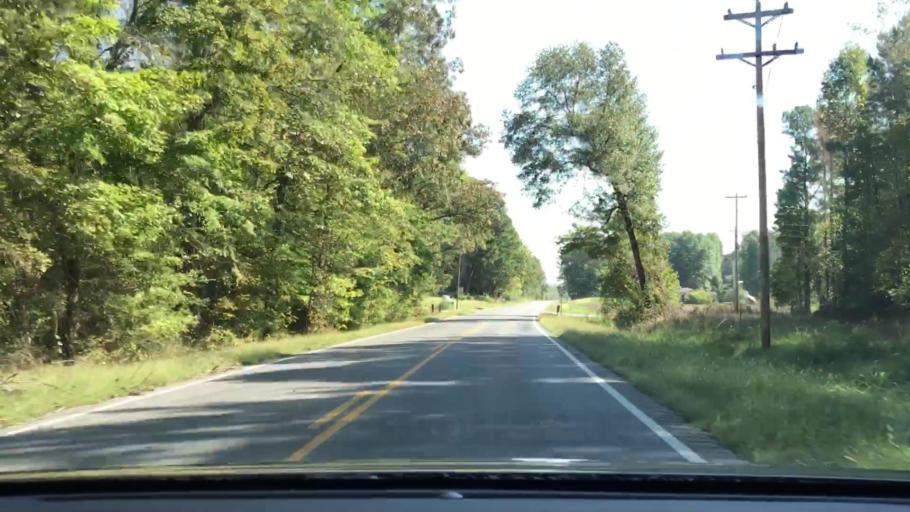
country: US
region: Kentucky
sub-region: Marshall County
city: Benton
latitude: 36.7648
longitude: -88.2460
